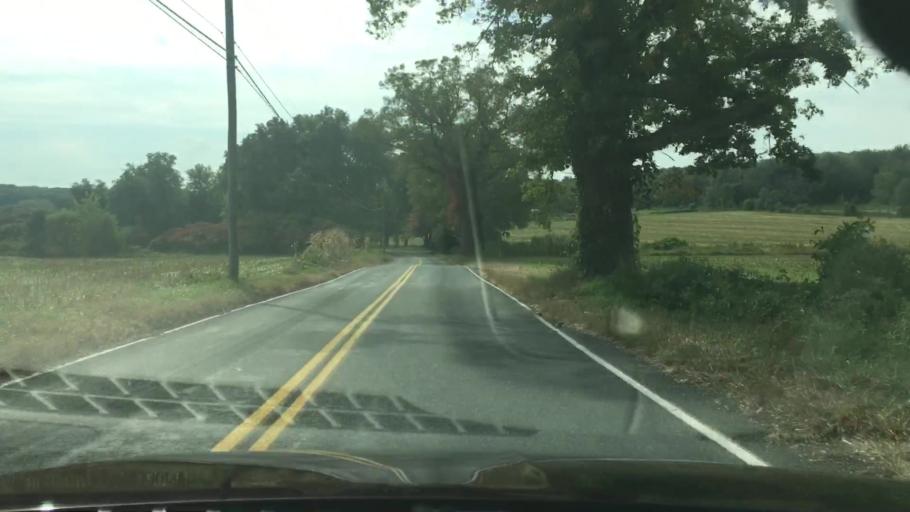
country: US
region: Connecticut
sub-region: Tolland County
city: Somers
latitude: 41.9633
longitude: -72.4830
